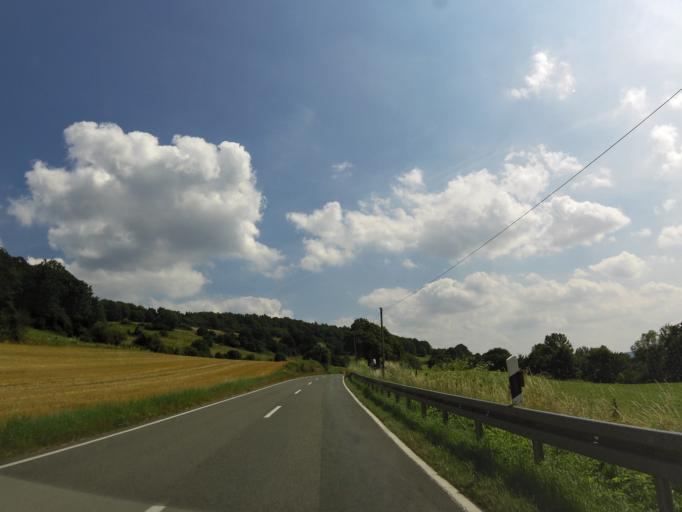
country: DE
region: Lower Saxony
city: Derental
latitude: 51.7023
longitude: 9.4045
